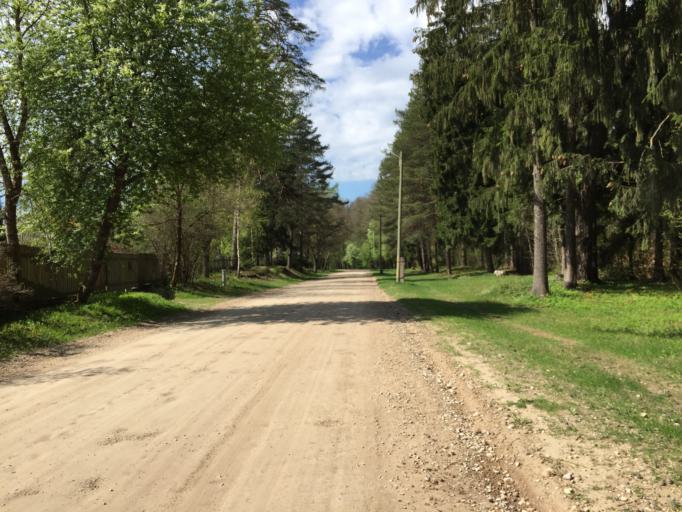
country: LV
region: Baldone
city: Baldone
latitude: 56.7414
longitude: 24.4100
